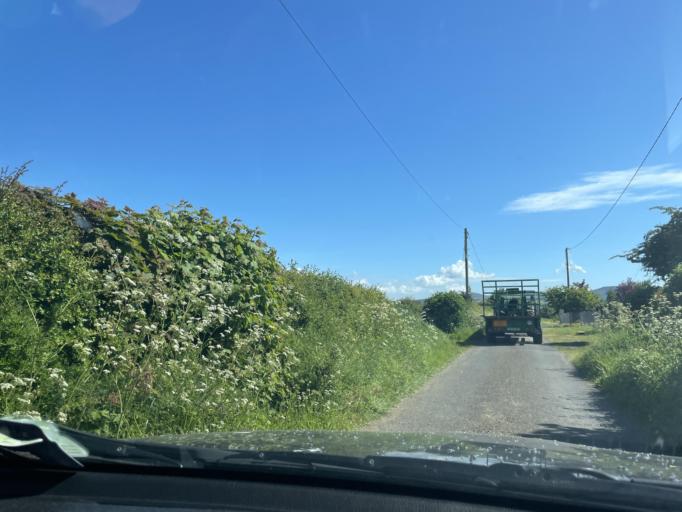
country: IE
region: Leinster
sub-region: County Carlow
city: Bagenalstown
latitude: 52.6334
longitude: -7.0154
